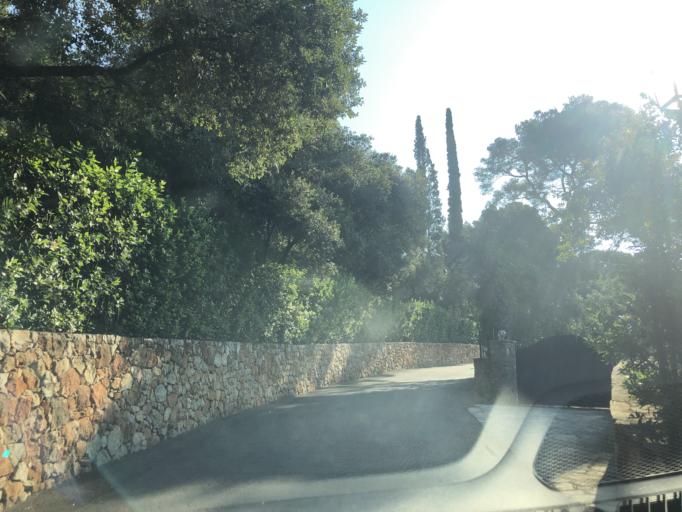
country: FR
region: Provence-Alpes-Cote d'Azur
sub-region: Departement des Alpes-Maritimes
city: Biot
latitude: 43.6230
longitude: 7.0910
